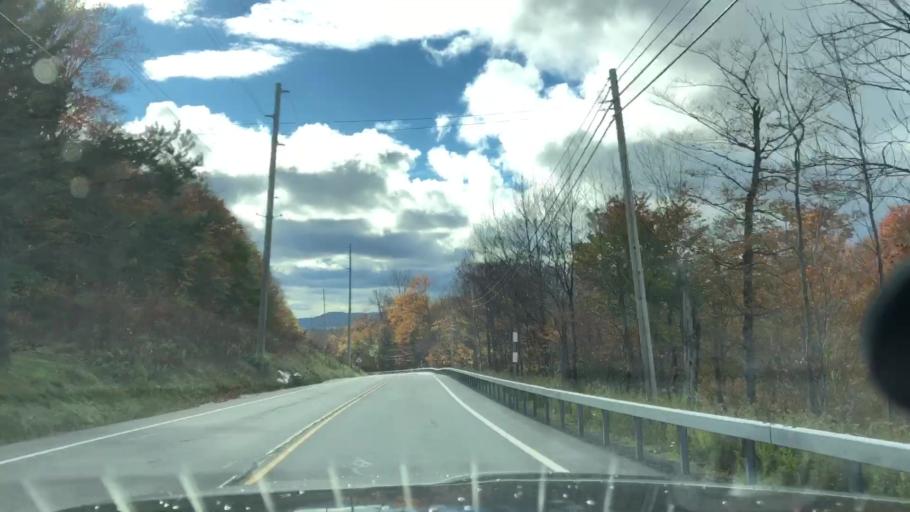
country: US
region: New York
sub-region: Oneida County
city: Boonville
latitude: 43.7236
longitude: -74.9400
